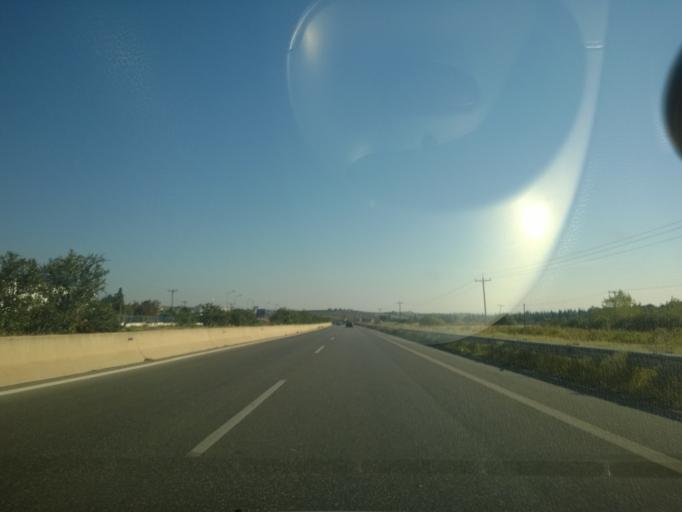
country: GR
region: Central Macedonia
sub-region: Nomos Chalkidikis
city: Lakkoma
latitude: 40.3698
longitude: 23.0455
